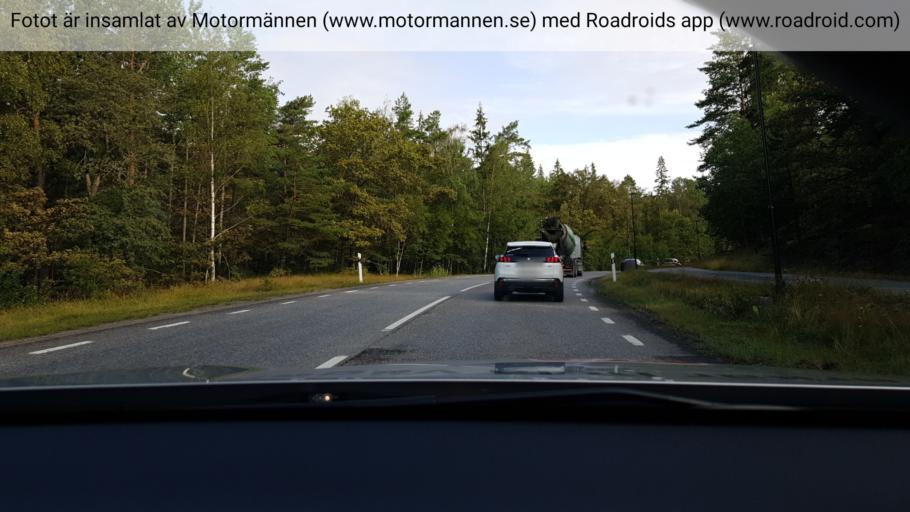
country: SE
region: Stockholm
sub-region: Huddinge Kommun
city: Huddinge
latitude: 59.2020
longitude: 18.0058
